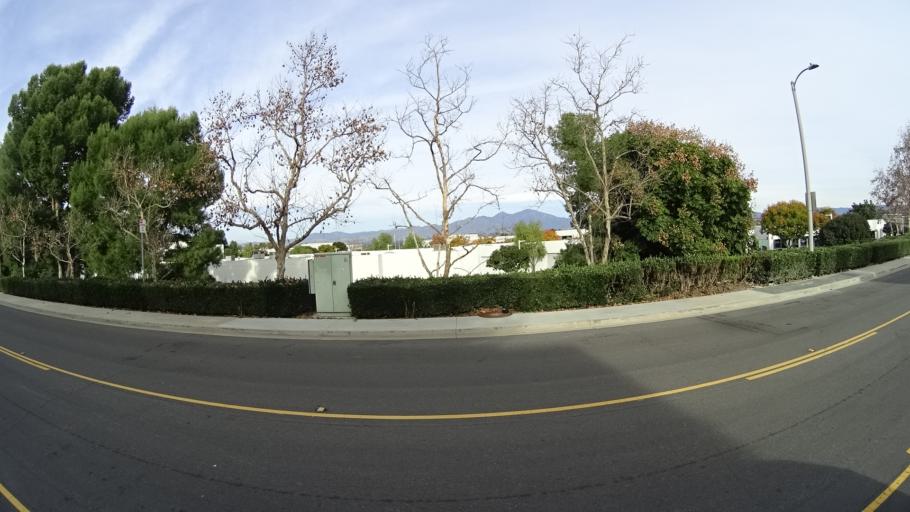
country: US
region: California
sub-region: Orange County
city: Aliso Viejo
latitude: 33.5677
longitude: -117.7257
